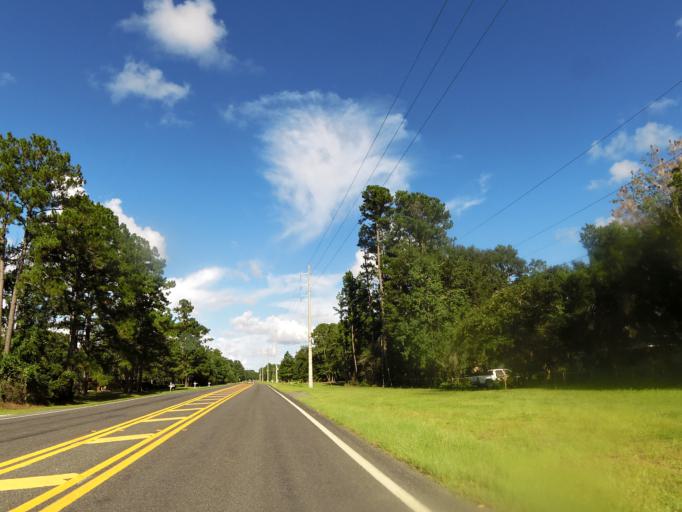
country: US
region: Georgia
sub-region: Camden County
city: Woodbine
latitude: 31.1050
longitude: -81.6826
